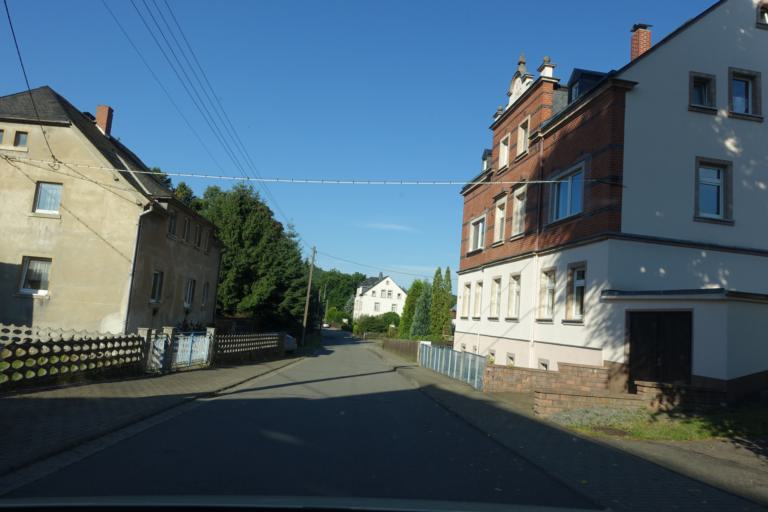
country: DE
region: Saxony
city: Falkenau
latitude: 50.8529
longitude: 13.1049
